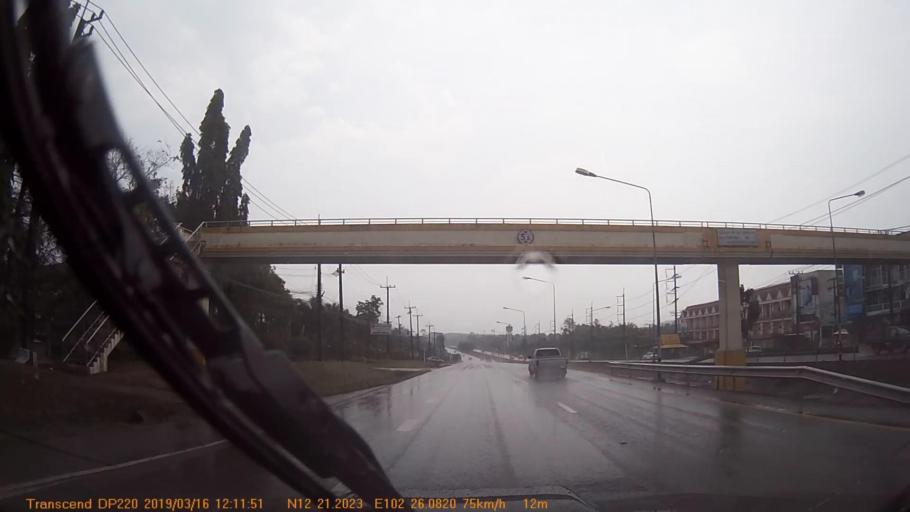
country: TH
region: Trat
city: Khao Saming
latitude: 12.3444
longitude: 102.4434
